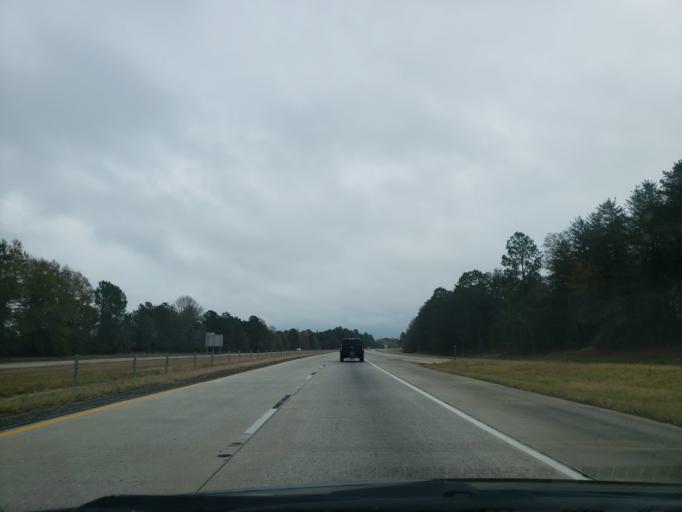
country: US
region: Georgia
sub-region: Treutlen County
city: Soperton
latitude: 32.4342
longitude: -82.6040
